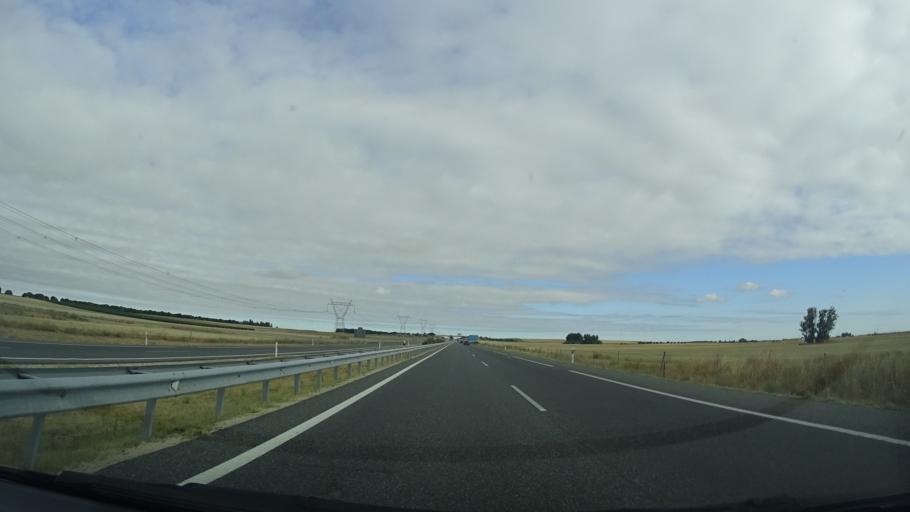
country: ES
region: Castille and Leon
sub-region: Provincia de Valladolid
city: San Pablo de la Moraleja
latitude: 41.1400
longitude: -4.7818
